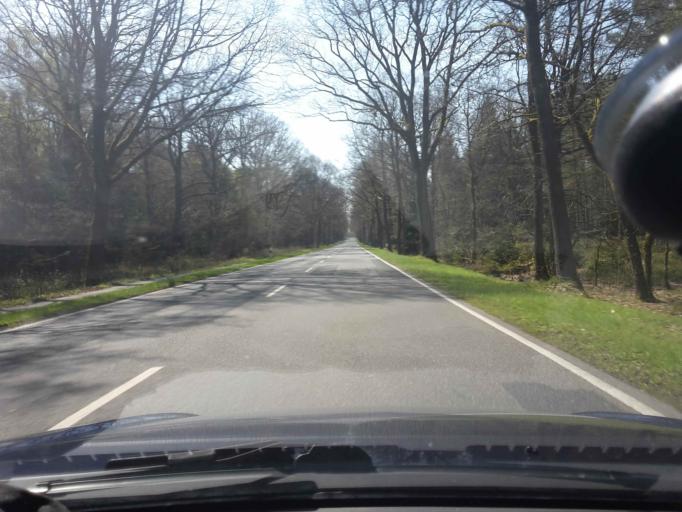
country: DE
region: Lower Saxony
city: Schneverdingen
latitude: 53.1455
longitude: 9.8453
